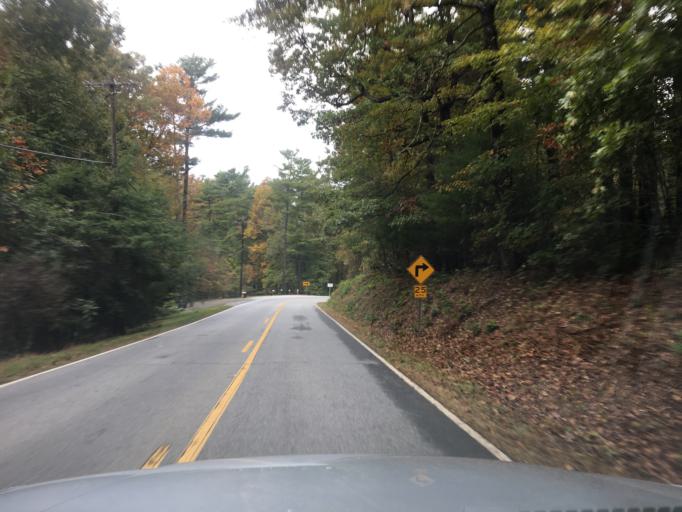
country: US
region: North Carolina
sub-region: Henderson County
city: Flat Rock
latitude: 35.2517
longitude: -82.4332
